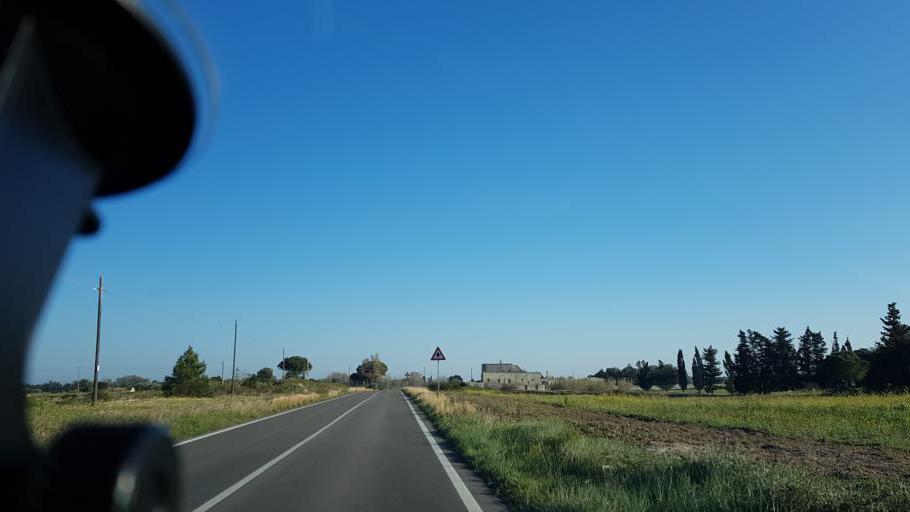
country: IT
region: Apulia
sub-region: Provincia di Lecce
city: Merine
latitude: 40.4148
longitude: 18.2528
